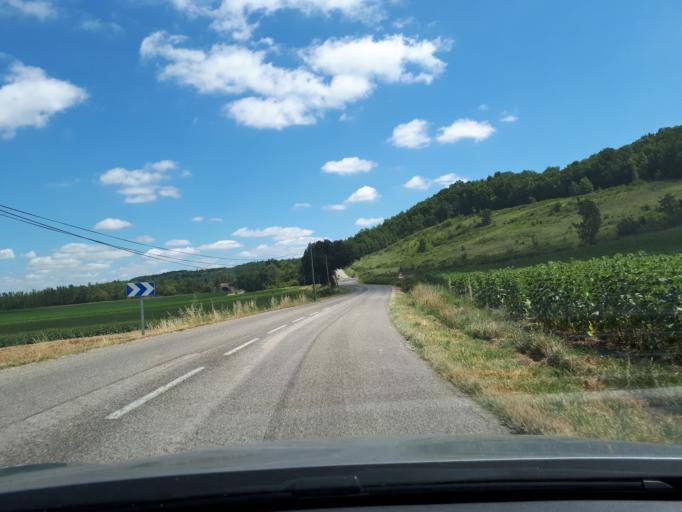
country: FR
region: Midi-Pyrenees
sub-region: Departement du Tarn-et-Garonne
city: Auvillar
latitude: 44.0544
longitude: 0.8629
